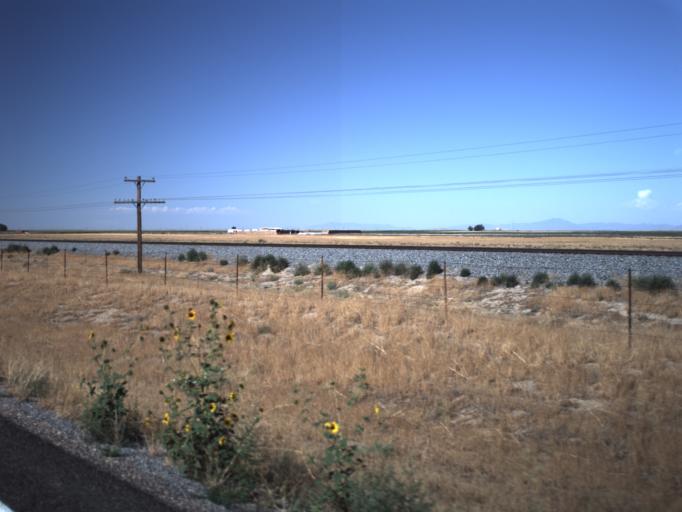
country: US
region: Utah
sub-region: Millard County
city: Delta
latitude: 39.5604
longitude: -112.3501
